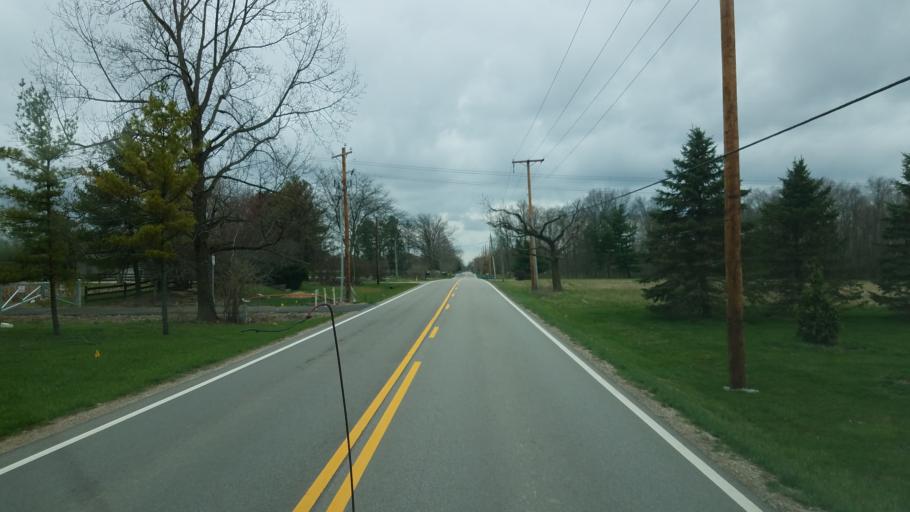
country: US
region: Ohio
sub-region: Delaware County
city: Powell
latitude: 40.2271
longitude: -83.1323
